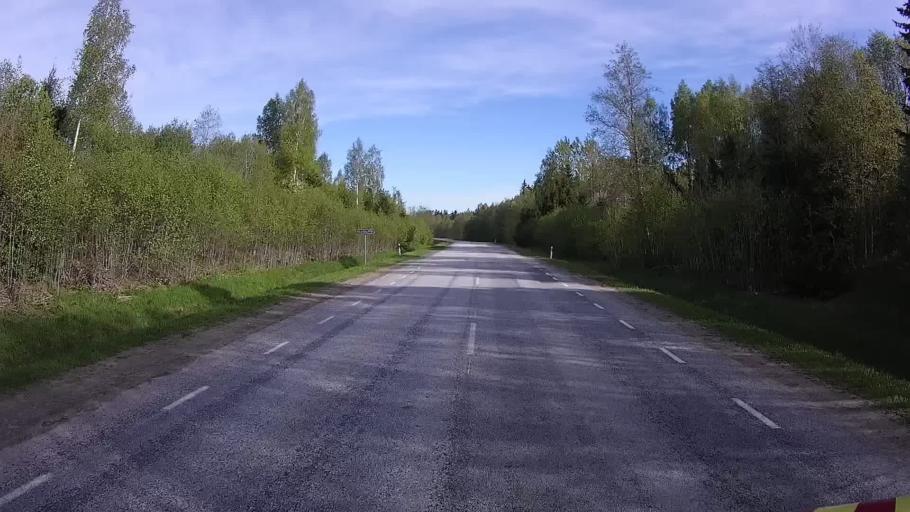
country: EE
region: Tartu
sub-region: Elva linn
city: Elva
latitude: 58.0768
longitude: 26.4984
